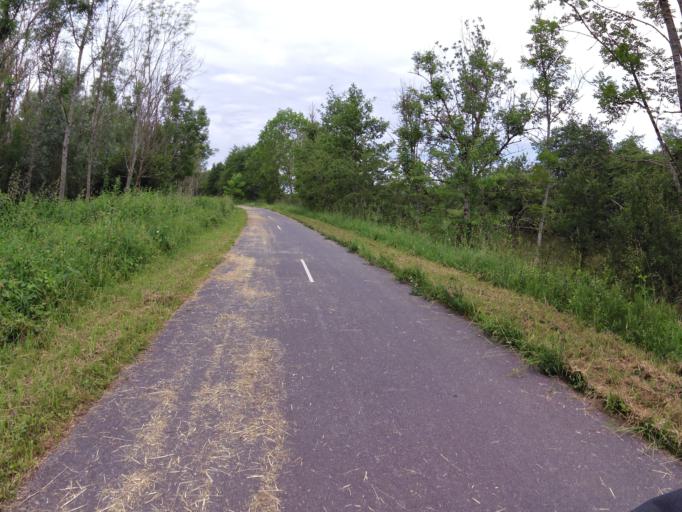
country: FR
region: Champagne-Ardenne
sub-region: Departement des Ardennes
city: Donchery
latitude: 49.6975
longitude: 4.8440
